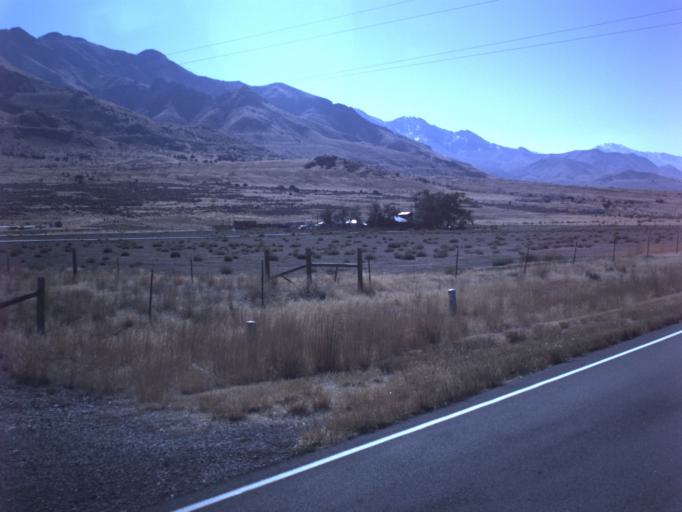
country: US
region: Utah
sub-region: Tooele County
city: Grantsville
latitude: 40.6874
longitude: -112.6694
